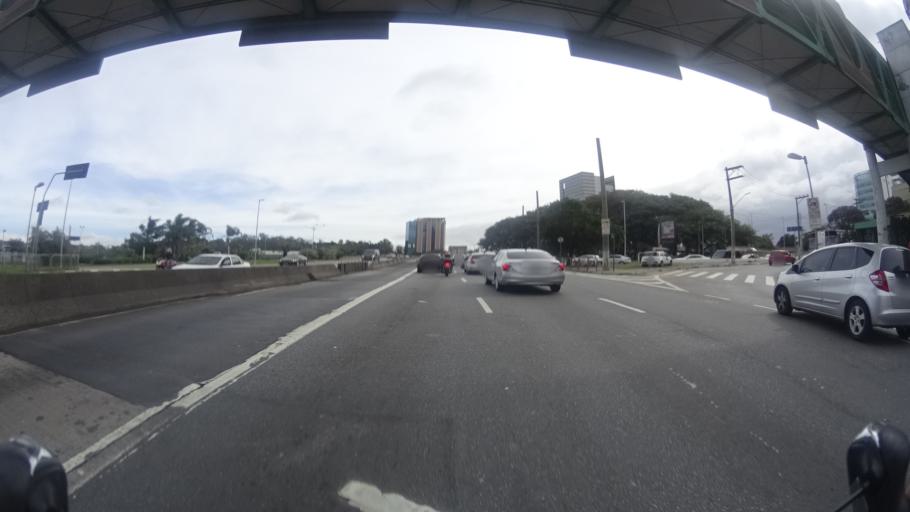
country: BR
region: Sao Paulo
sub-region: Sao Paulo
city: Sao Paulo
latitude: -23.5719
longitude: -46.6989
